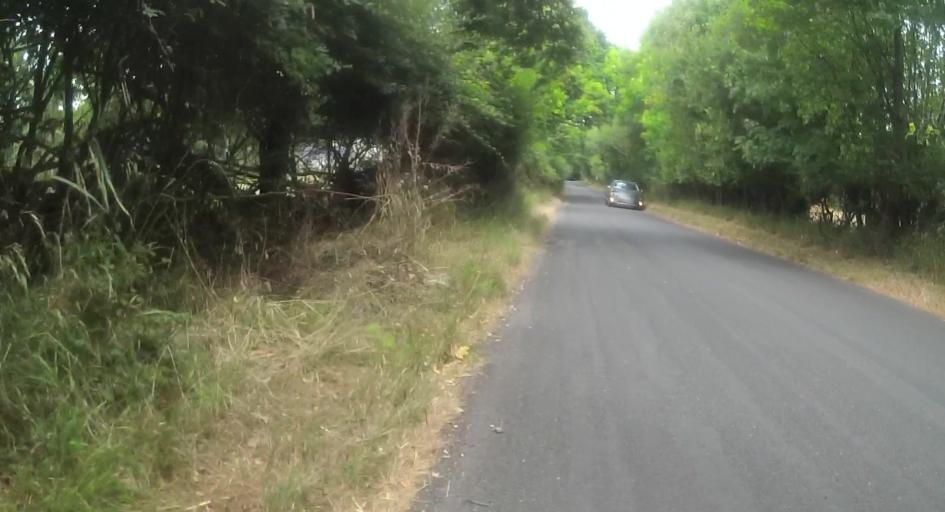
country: GB
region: England
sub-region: Dorset
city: Wareham
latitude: 50.6494
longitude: -2.0975
